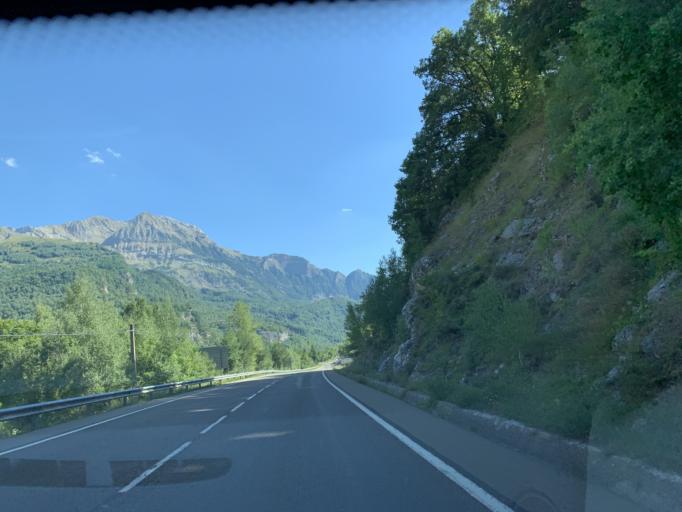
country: ES
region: Aragon
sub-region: Provincia de Huesca
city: Hoz de Jaca
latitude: 42.7243
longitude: -0.3068
